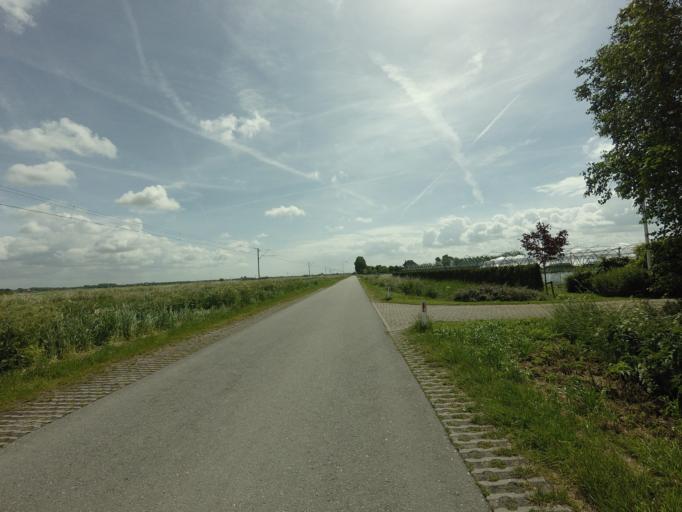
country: NL
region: North Holland
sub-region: Gemeente Opmeer
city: Opmeer
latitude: 52.6603
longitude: 4.9773
